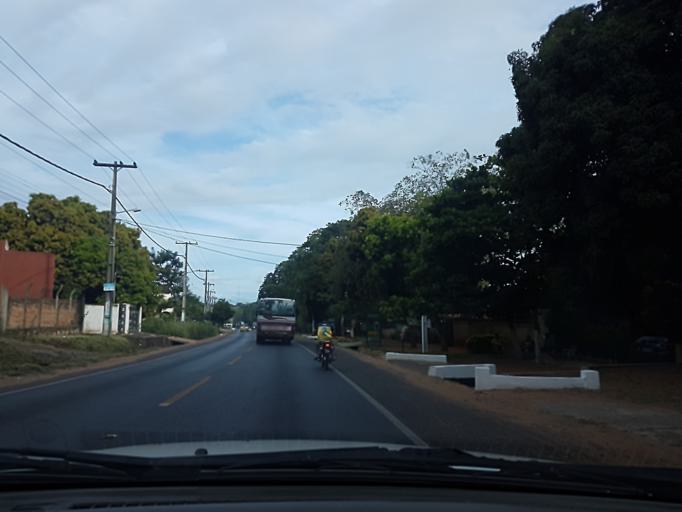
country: PY
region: Central
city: San Lorenzo
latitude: -25.2821
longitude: -57.4702
